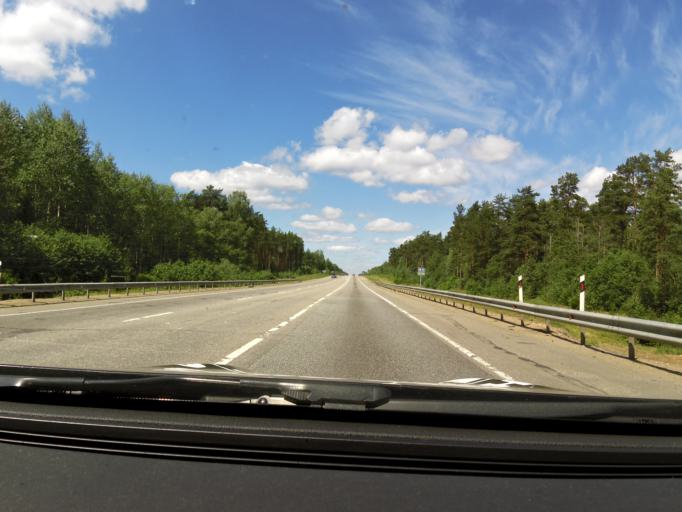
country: RU
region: Tverskaya
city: Kuzhenkino
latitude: 57.8153
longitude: 33.8347
